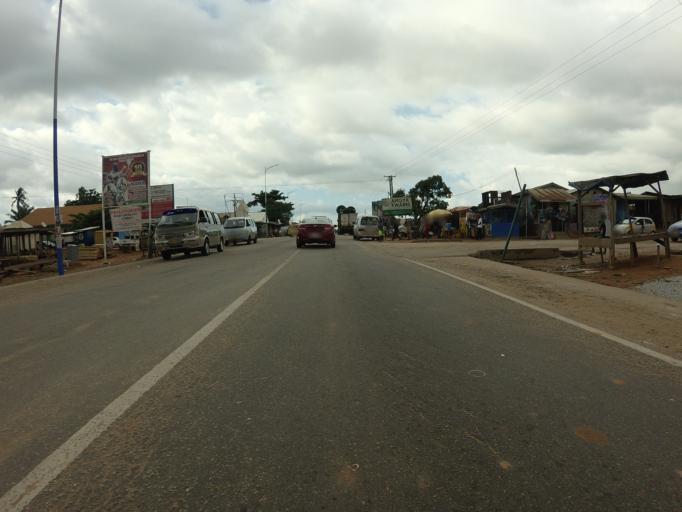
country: GH
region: Ashanti
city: Tafo
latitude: 6.8131
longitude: -1.6489
